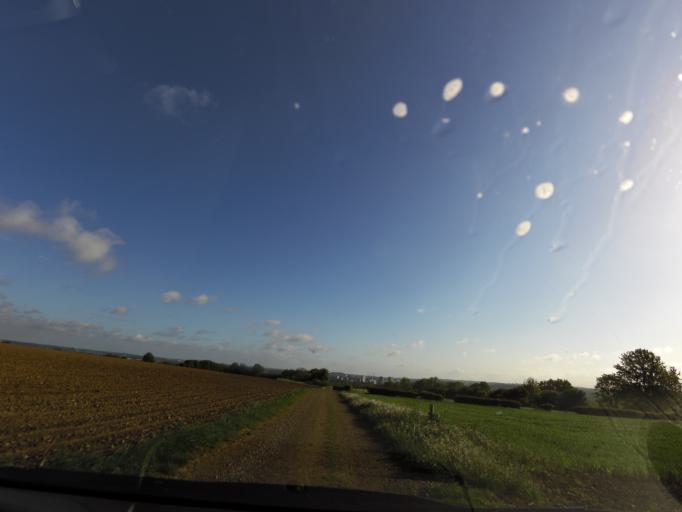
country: NL
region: Limburg
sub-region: Gemeente Voerendaal
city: Ubachsberg
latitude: 50.8651
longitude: 5.9562
